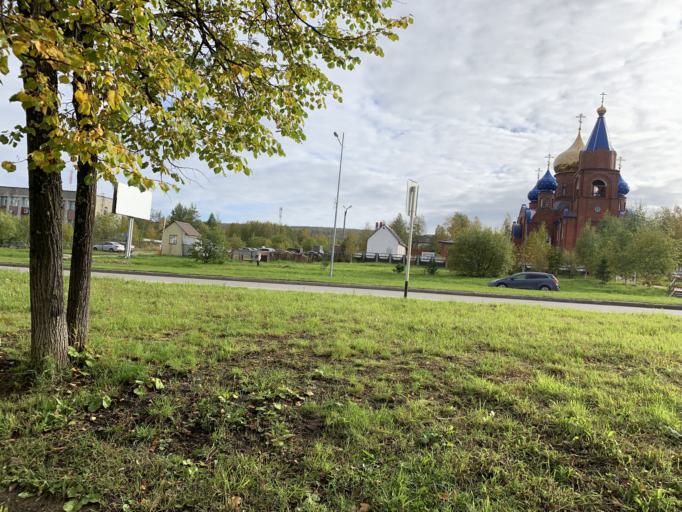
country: RU
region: Perm
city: Gubakha
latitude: 58.8341
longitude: 57.5561
